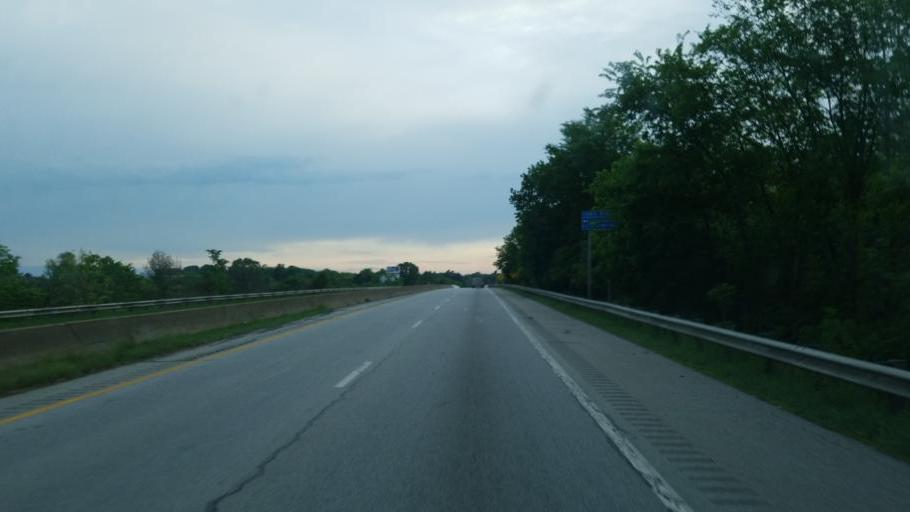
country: US
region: Ohio
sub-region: Wayne County
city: Dalton
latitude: 40.7988
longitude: -81.7403
